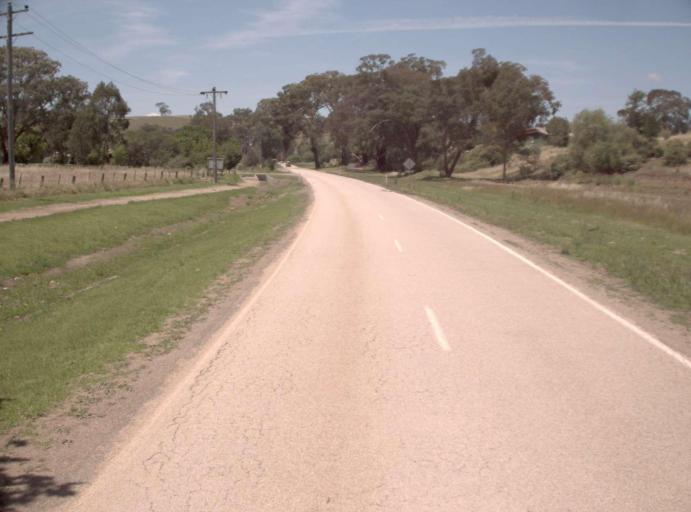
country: AU
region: Victoria
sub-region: East Gippsland
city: Bairnsdale
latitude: -37.2715
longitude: 147.7262
